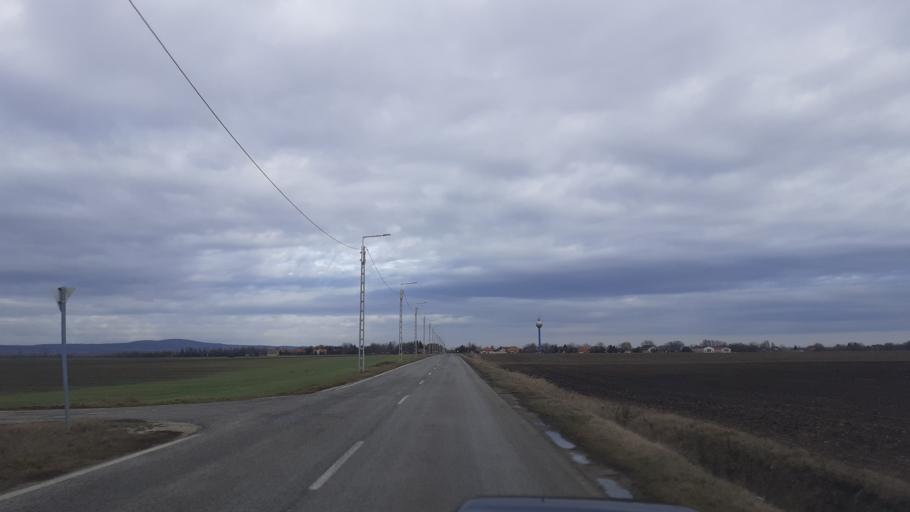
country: HU
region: Fejer
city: Pakozd
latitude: 47.1613
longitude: 18.5101
